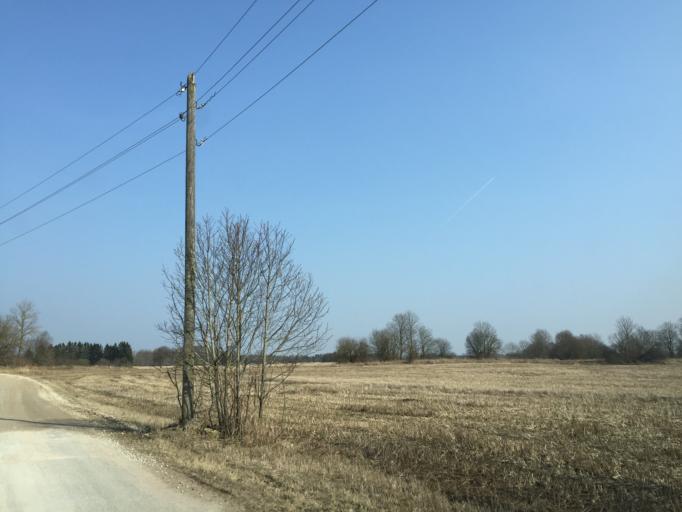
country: EE
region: Saare
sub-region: Kuressaare linn
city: Kuressaare
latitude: 58.3719
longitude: 22.6874
